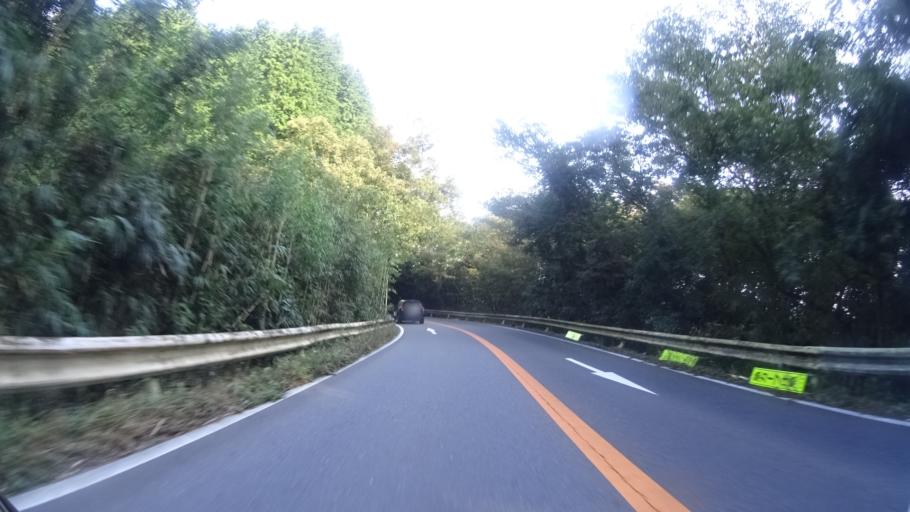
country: JP
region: Oita
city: Beppu
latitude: 33.2691
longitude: 131.4364
